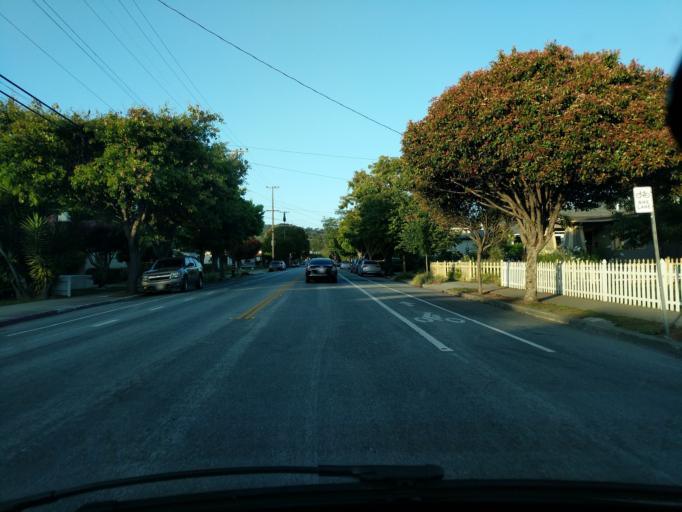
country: US
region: California
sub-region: Alameda County
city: San Leandro
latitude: 37.7284
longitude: -122.1437
